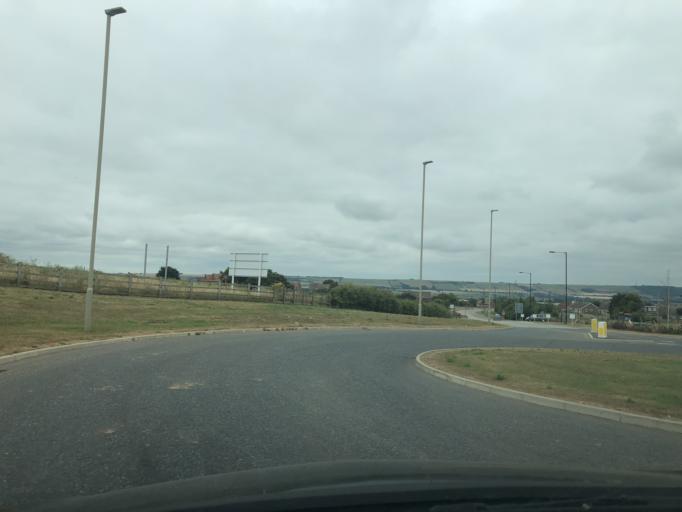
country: GB
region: England
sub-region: North Yorkshire
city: Scarborough
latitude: 54.2476
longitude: -0.3839
